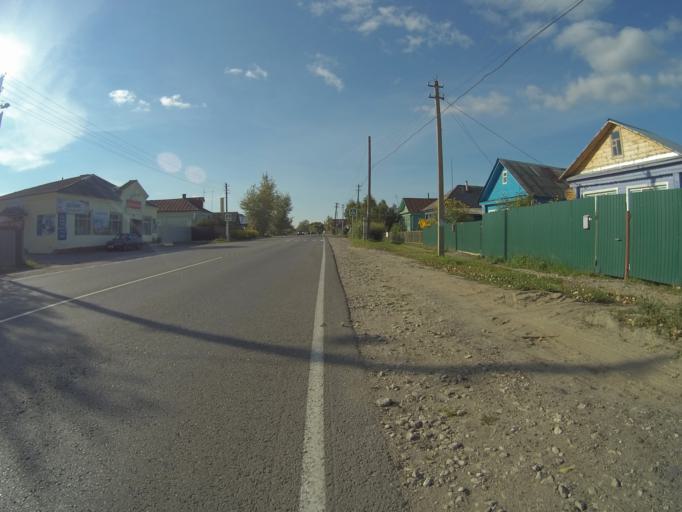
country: RU
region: Vladimir
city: Kommunar
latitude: 56.0417
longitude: 40.5461
